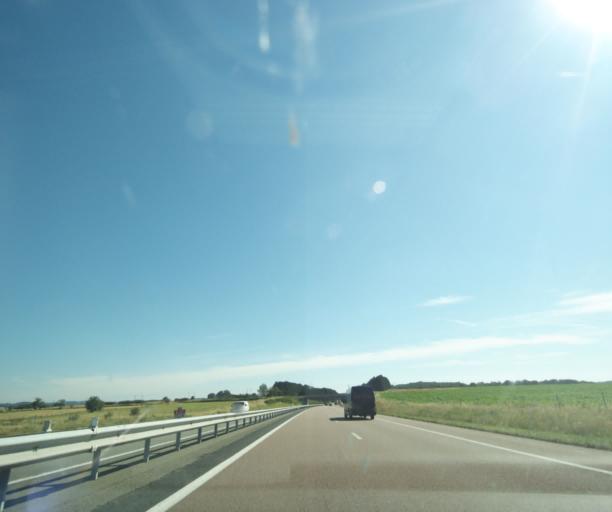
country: FR
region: Champagne-Ardenne
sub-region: Departement de la Haute-Marne
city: Saulxures
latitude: 48.0760
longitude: 5.6035
